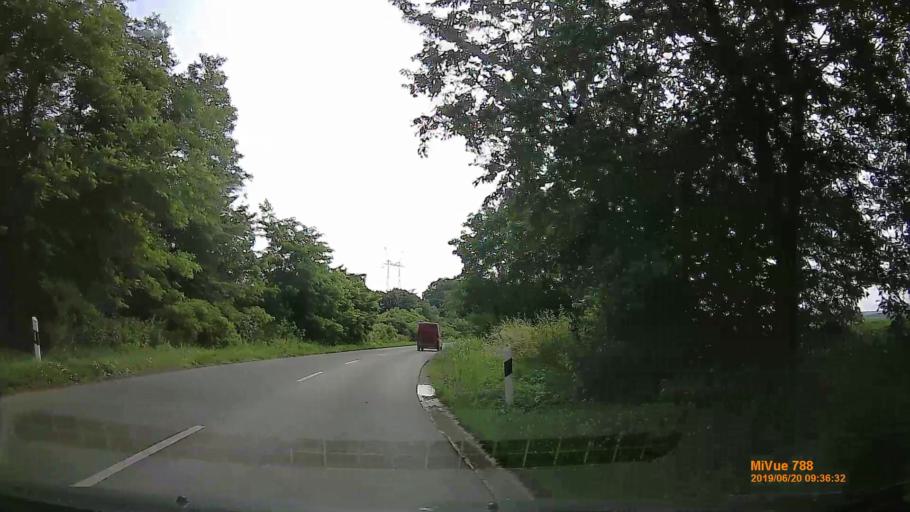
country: HU
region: Baranya
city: Pecsvarad
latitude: 46.1687
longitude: 18.4520
